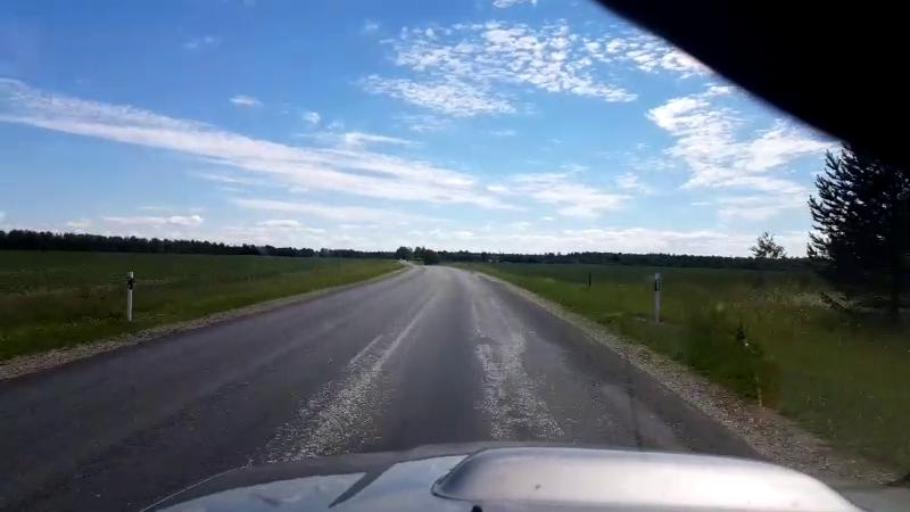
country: EE
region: Laeaene-Virumaa
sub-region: Rakke vald
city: Rakke
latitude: 58.8968
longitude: 26.2831
